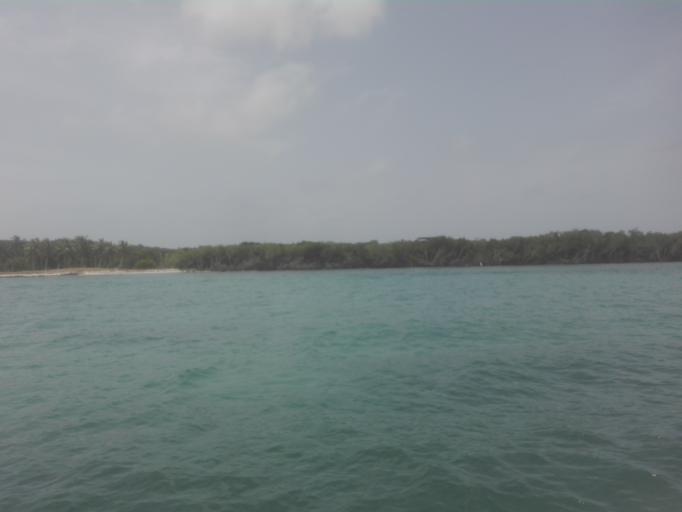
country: CO
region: Bolivar
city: Turbana
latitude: 10.1568
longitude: -75.6875
